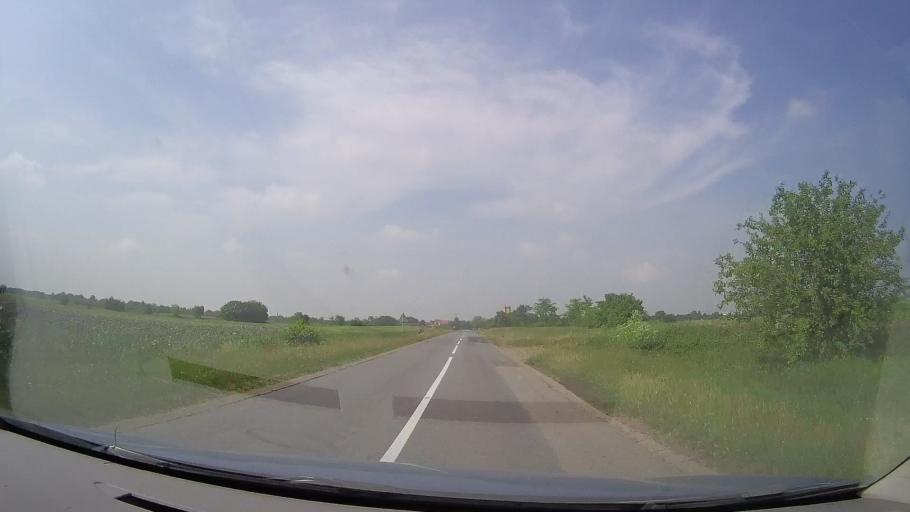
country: RS
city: Padina
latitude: 45.1352
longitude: 20.7356
